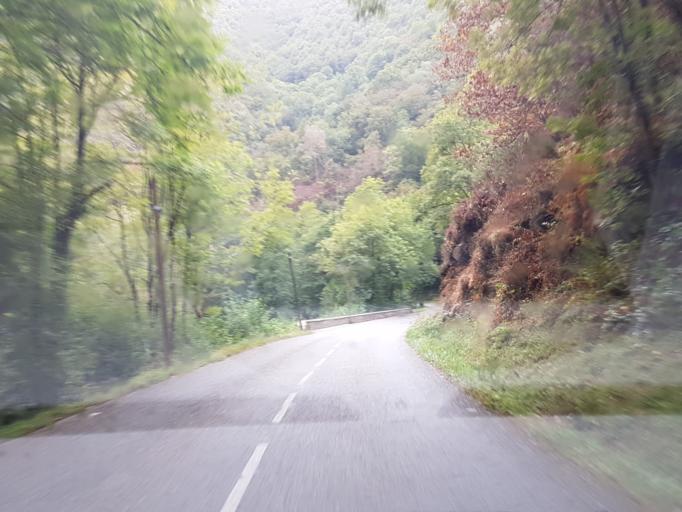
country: FR
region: Midi-Pyrenees
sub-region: Departement de l'Ariege
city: Saint-Girons
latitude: 42.9101
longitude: 1.2719
